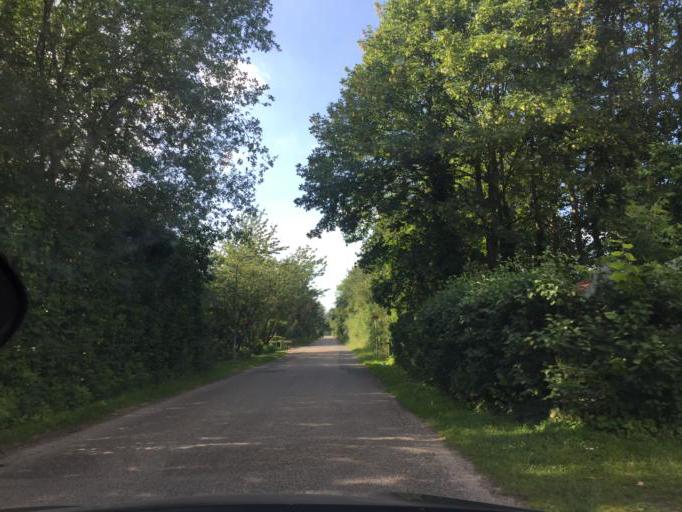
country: DK
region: South Denmark
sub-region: Kerteminde Kommune
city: Langeskov
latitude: 55.3189
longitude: 10.5298
